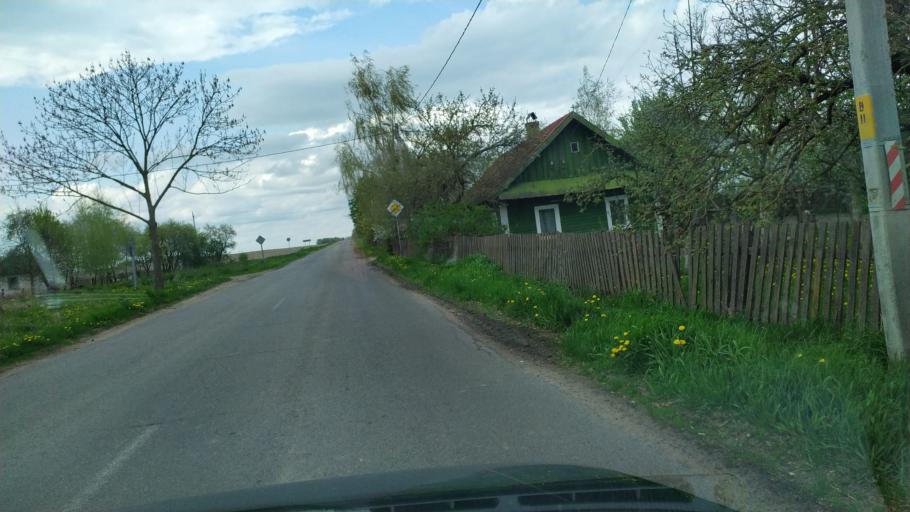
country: BY
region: Brest
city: Pruzhany
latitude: 52.6532
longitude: 24.3833
